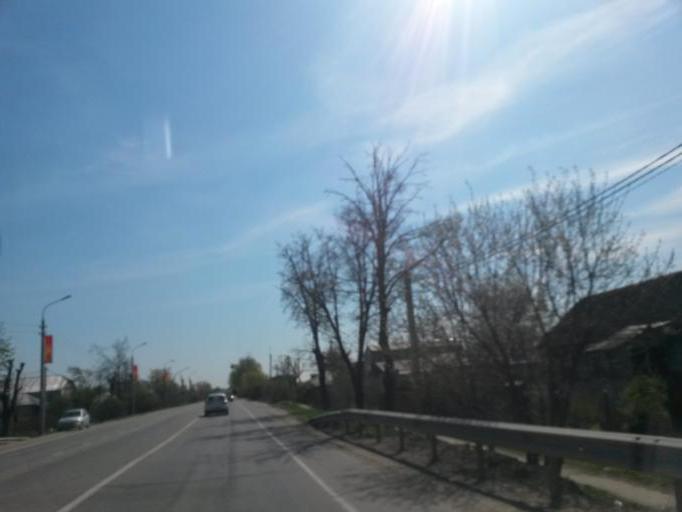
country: RU
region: Moskovskaya
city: Stolbovaya
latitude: 55.2805
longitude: 37.5103
